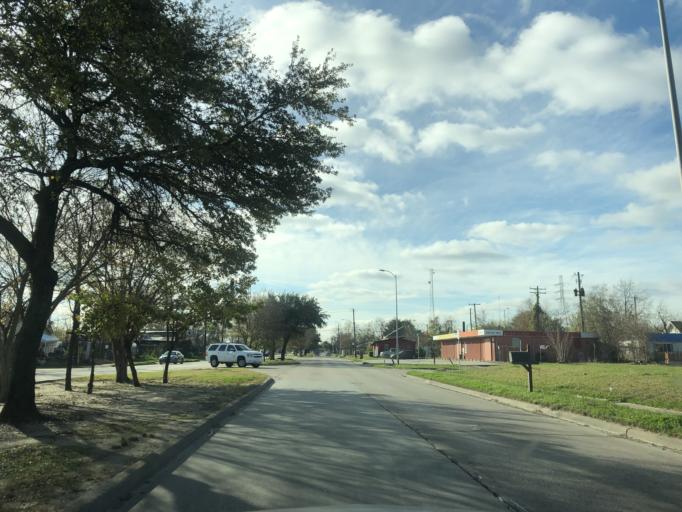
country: US
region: Texas
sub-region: Harris County
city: Jacinto City
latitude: 29.8100
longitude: -95.2846
